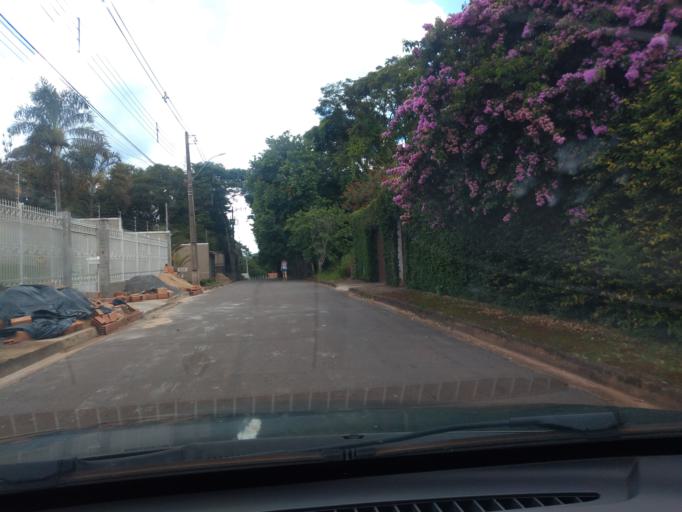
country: BR
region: Minas Gerais
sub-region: Tres Coracoes
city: Tres Coracoes
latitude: -21.6874
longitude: -45.2669
